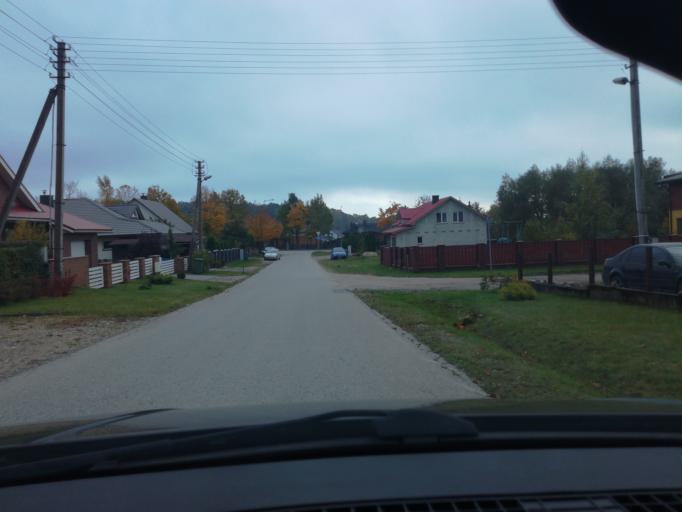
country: LT
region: Alytaus apskritis
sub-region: Alytus
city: Alytus
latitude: 54.3936
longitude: 24.0030
